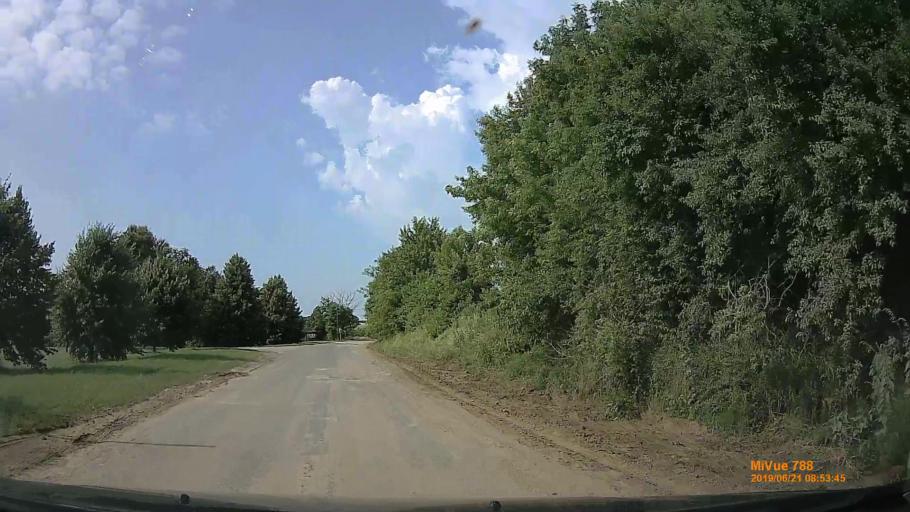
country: HU
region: Baranya
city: Buekkoesd
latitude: 46.1688
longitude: 17.8884
